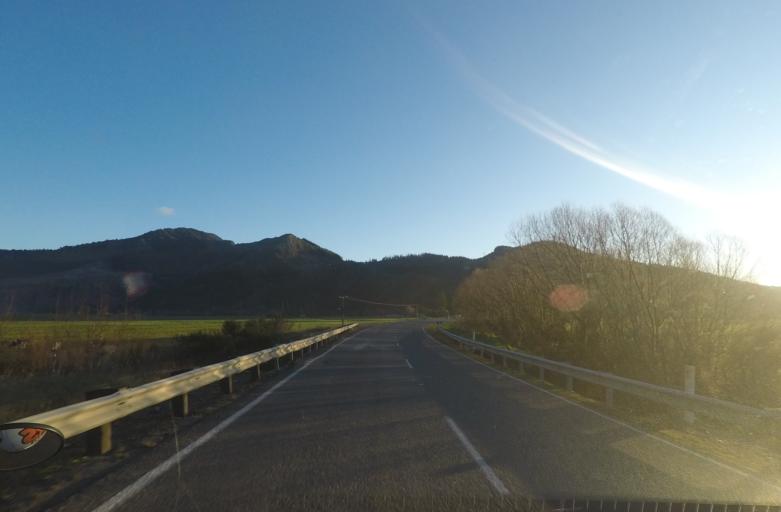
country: NZ
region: Marlborough
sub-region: Marlborough District
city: Picton
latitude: -41.2912
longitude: 173.6751
